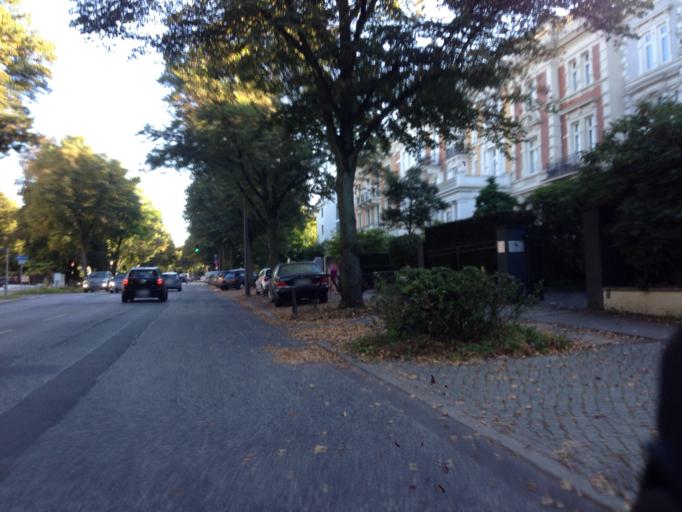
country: DE
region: Hamburg
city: Hamburg-Nord
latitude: 53.5799
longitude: 9.9887
